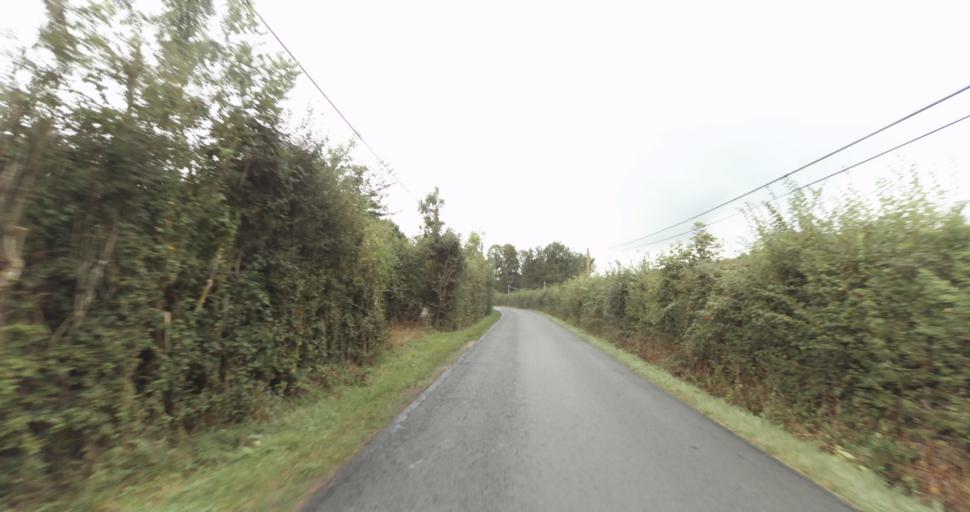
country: FR
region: Lower Normandy
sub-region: Departement de l'Orne
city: Vimoutiers
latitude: 48.9114
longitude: 0.1983
